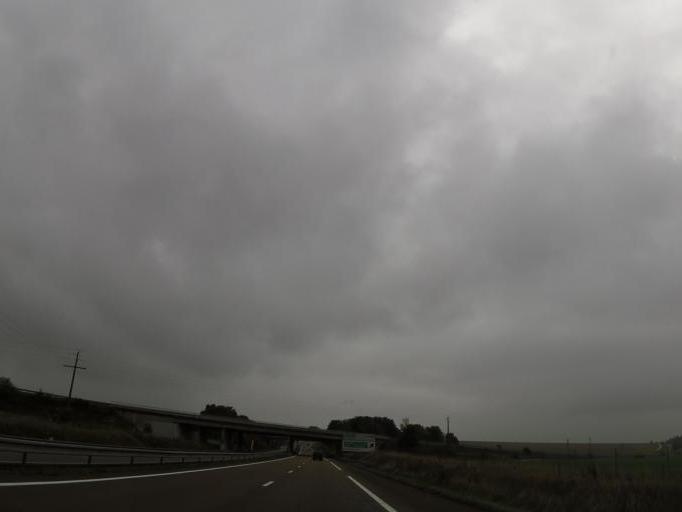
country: FR
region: Champagne-Ardenne
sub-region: Departement de la Marne
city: Fagnieres
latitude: 49.0474
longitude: 4.3038
